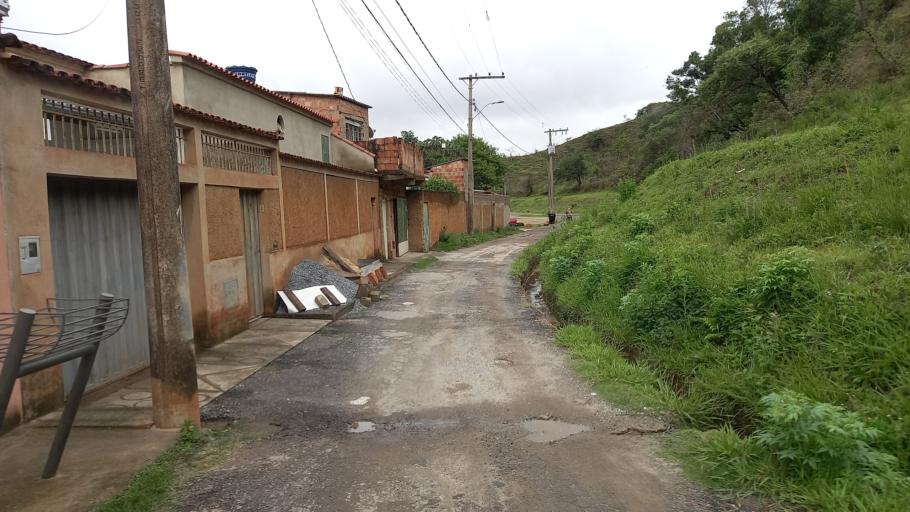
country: BR
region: Minas Gerais
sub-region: Belo Horizonte
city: Belo Horizonte
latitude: -19.9214
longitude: -43.8859
